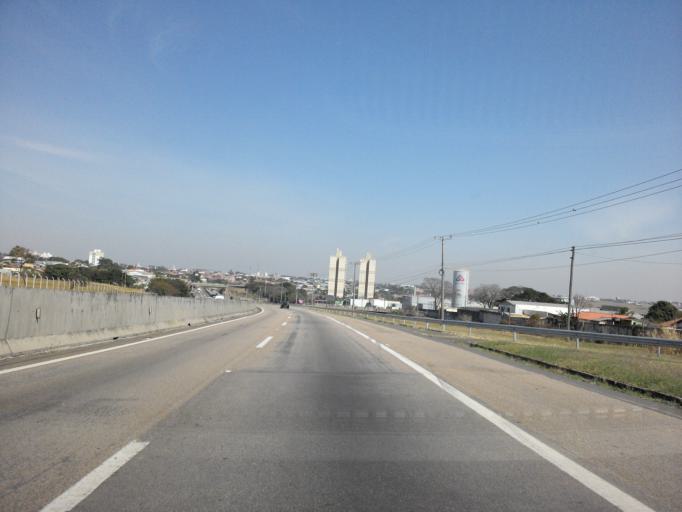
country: BR
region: Sao Paulo
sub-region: Hortolandia
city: Hortolandia
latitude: -22.8862
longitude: -47.1595
